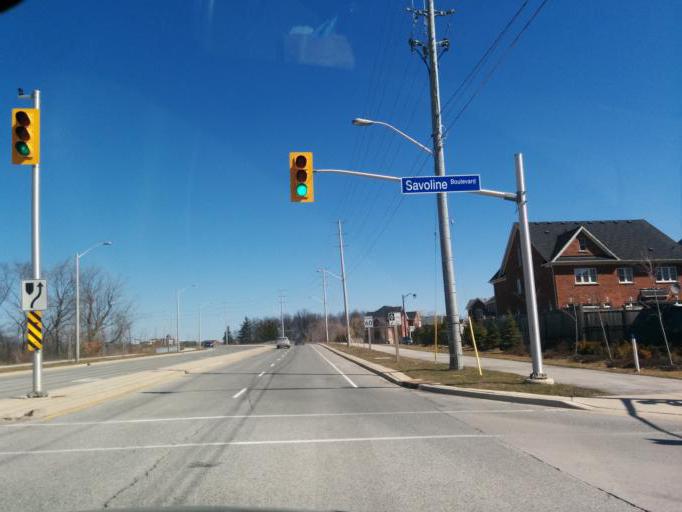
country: CA
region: Ontario
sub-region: Halton
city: Milton
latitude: 43.4976
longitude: -79.8946
